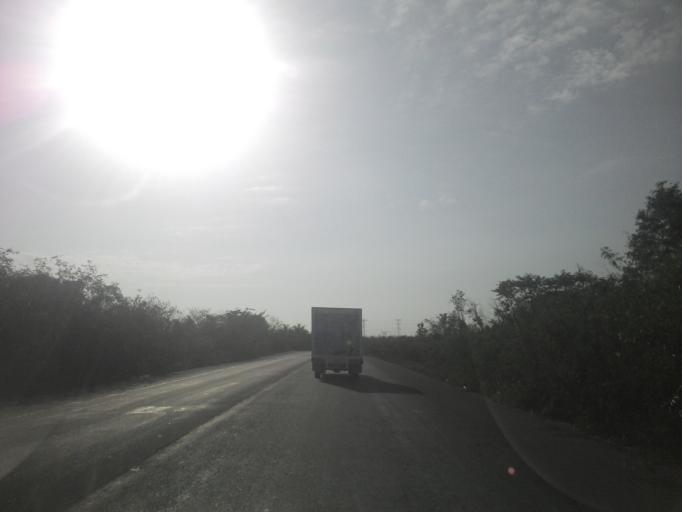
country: MX
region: Yucatan
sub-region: Valladolid
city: Tesoco
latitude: 20.7113
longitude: -88.1650
